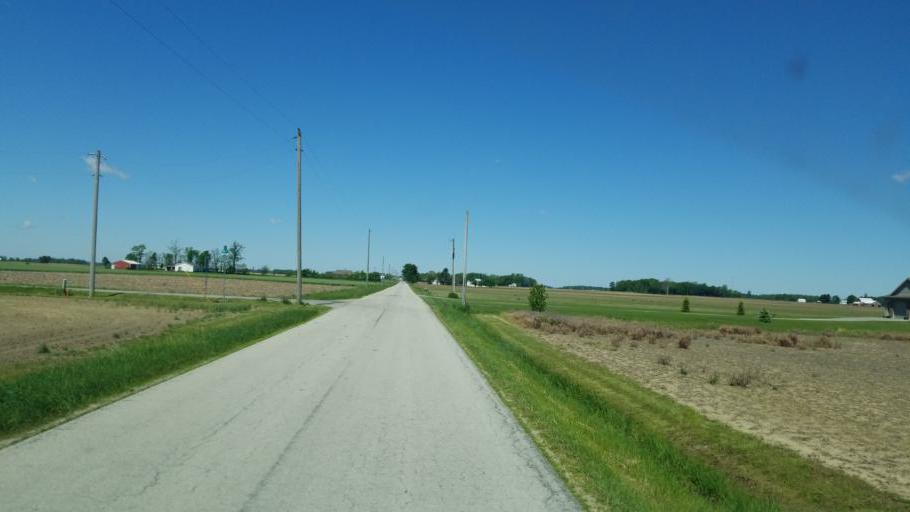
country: US
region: Ohio
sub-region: Shelby County
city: Jackson Center
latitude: 40.4175
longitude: -84.0062
